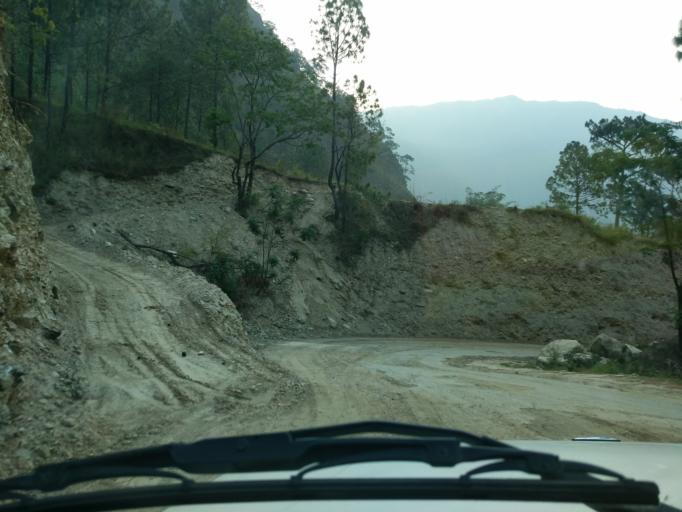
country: BT
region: Mongar
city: Mongar
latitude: 27.2608
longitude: 91.1812
